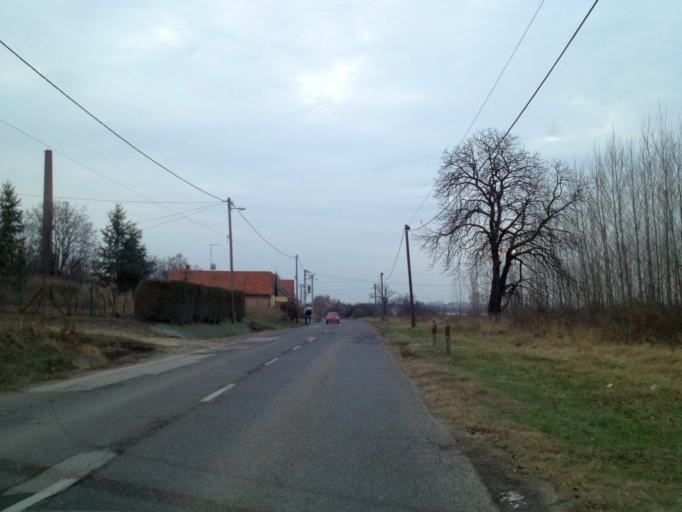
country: HU
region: Heves
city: Hatvan
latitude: 47.6843
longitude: 19.6883
